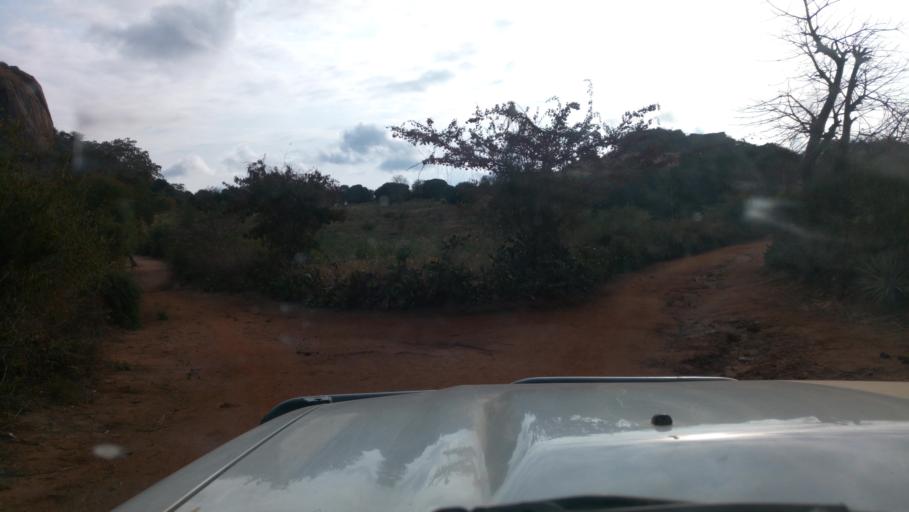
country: KE
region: Kitui
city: Kitui
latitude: -1.8940
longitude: 38.2439
